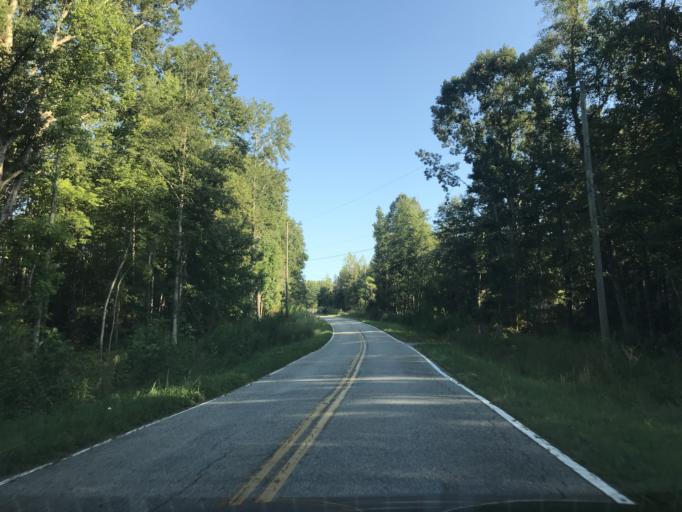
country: US
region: South Carolina
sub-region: Spartanburg County
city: Mayo
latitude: 35.1211
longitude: -81.7894
